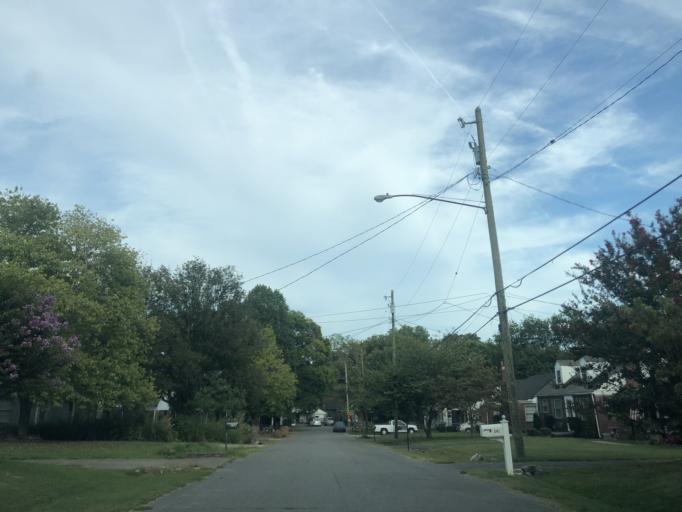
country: US
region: Tennessee
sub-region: Davidson County
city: Oak Hill
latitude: 36.1024
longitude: -86.7362
